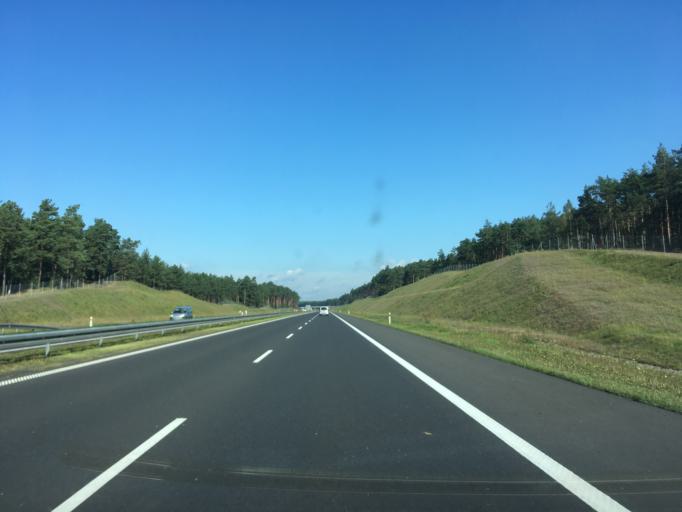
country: PL
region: Kujawsko-Pomorskie
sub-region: Powiat swiecki
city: Warlubie
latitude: 53.4826
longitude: 18.6168
